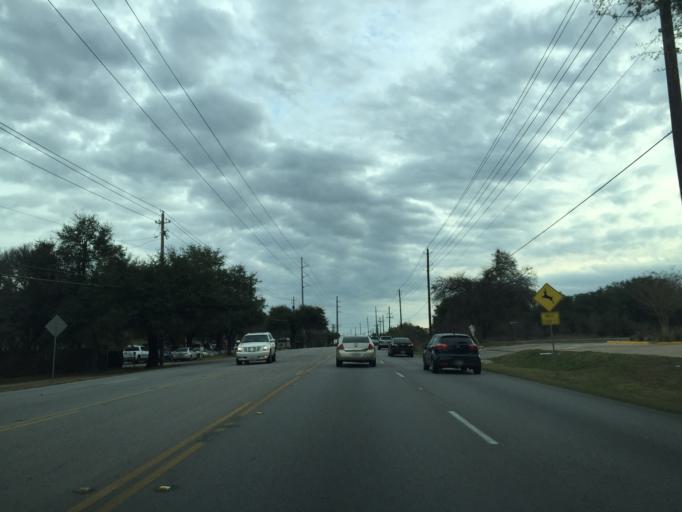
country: US
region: Texas
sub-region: Williamson County
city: Jollyville
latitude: 30.4383
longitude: -97.7576
